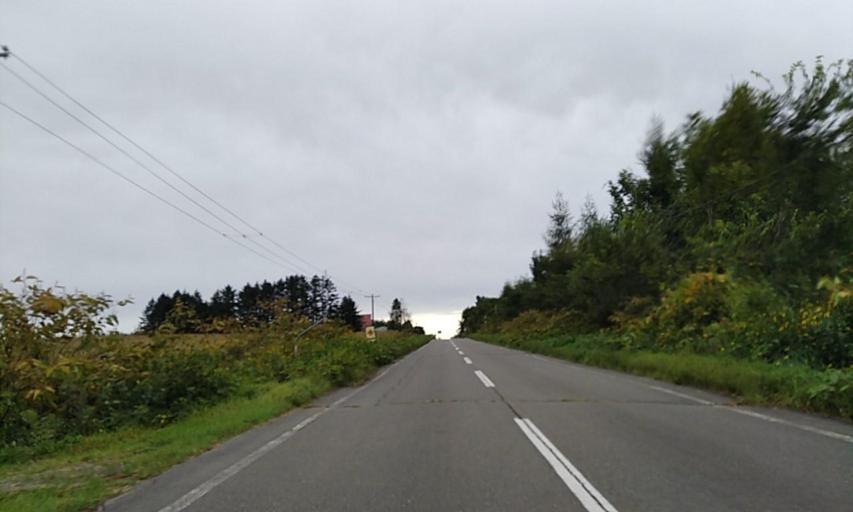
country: JP
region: Hokkaido
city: Obihiro
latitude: 42.6640
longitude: 143.0700
